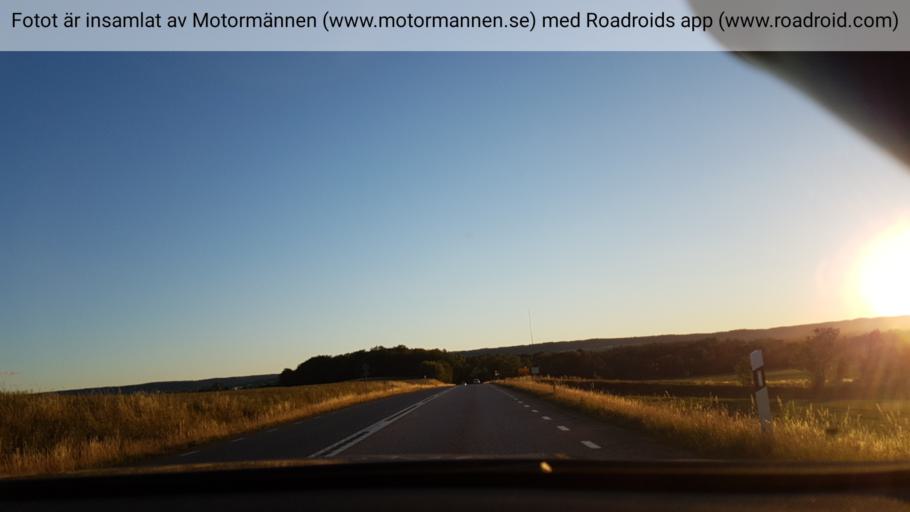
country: SE
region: Vaestra Goetaland
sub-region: Skovde Kommun
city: Skoevde
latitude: 58.3983
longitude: 13.9139
